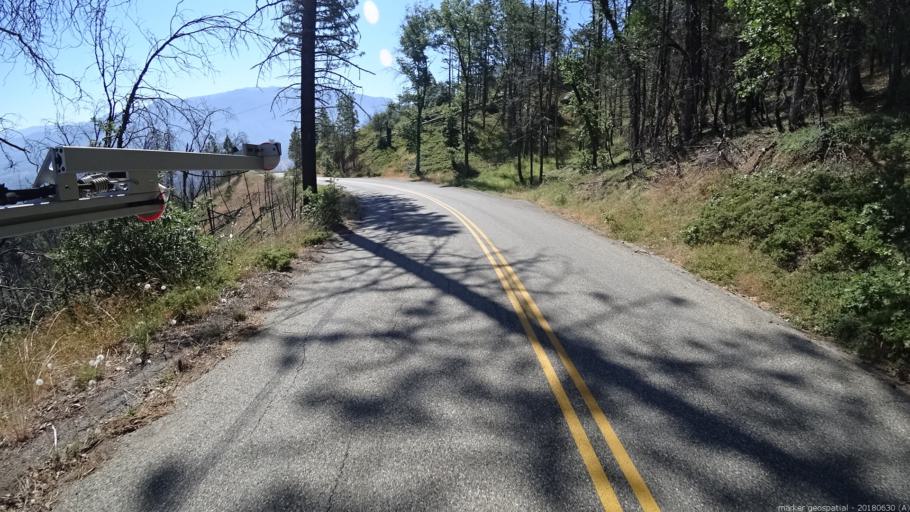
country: US
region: California
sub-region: Fresno County
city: Auberry
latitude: 37.2998
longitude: -119.3494
